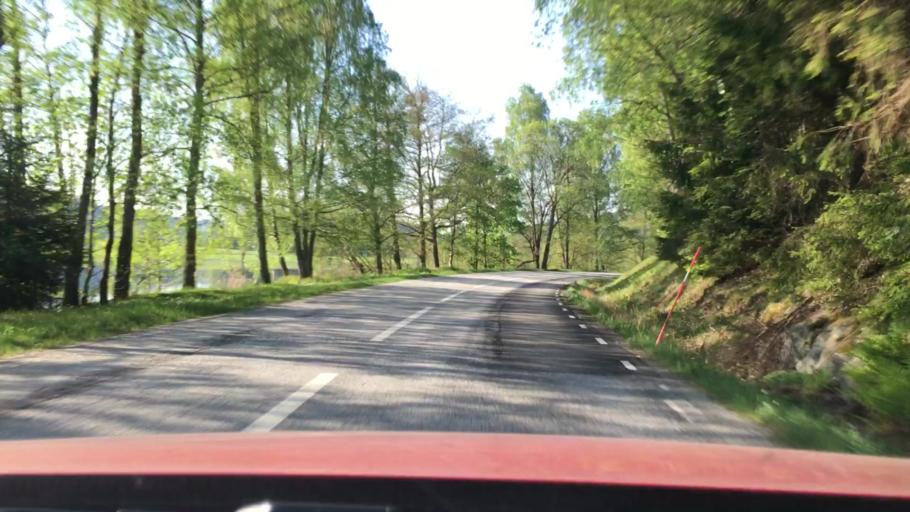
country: SE
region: Vaestra Goetaland
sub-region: Munkedals Kommun
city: Munkedal
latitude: 58.6254
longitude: 11.5601
